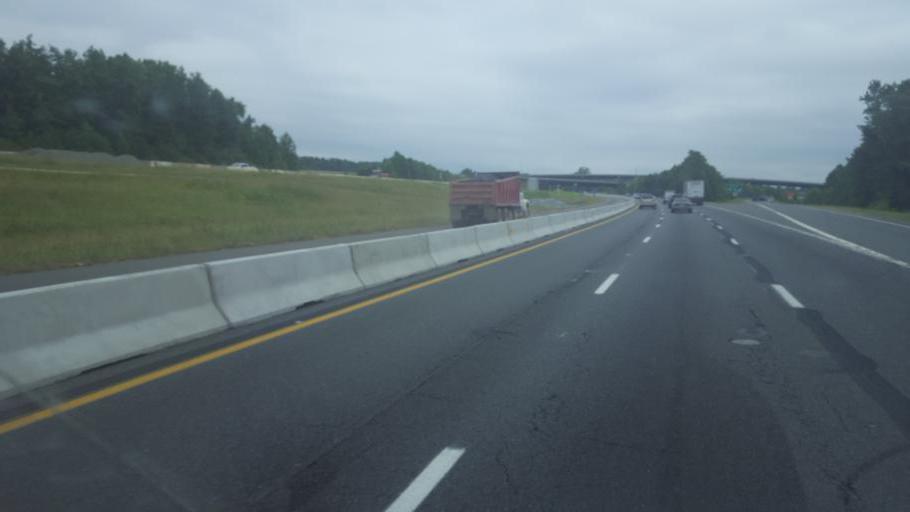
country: US
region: North Carolina
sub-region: Mecklenburg County
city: Huntersville
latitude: 35.3586
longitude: -80.8430
